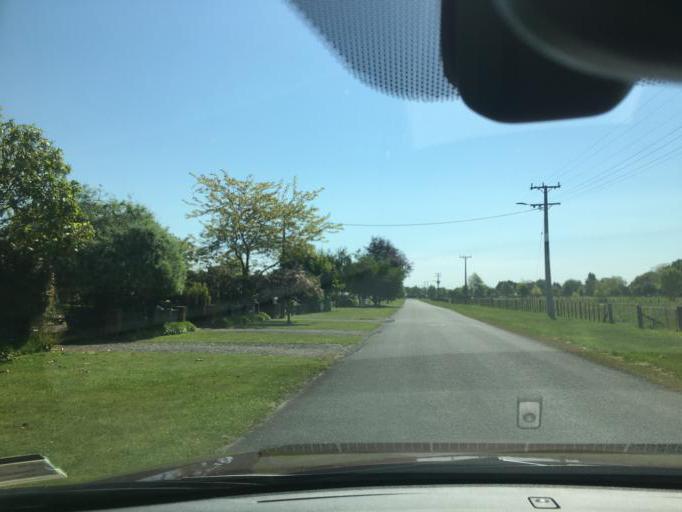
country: NZ
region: Waikato
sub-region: Waipa District
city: Cambridge
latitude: -37.9188
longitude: 175.4684
